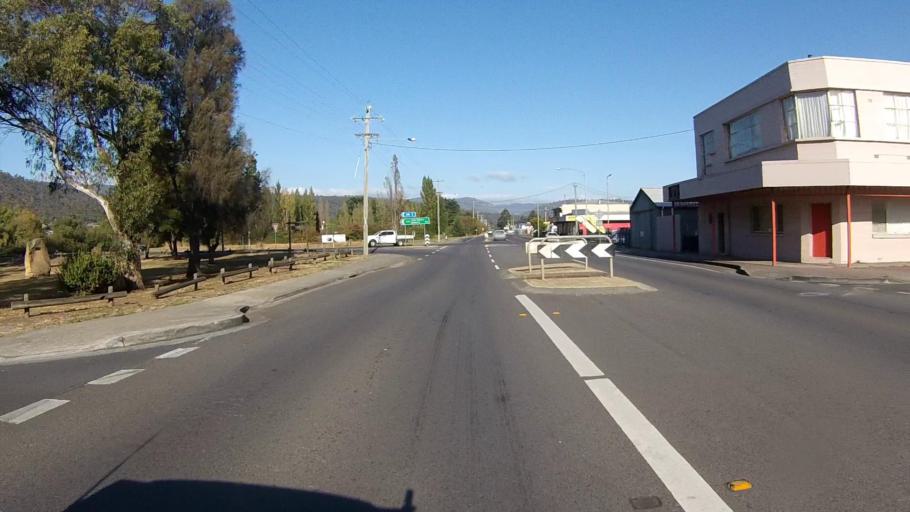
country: AU
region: Tasmania
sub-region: Derwent Valley
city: New Norfolk
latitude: -42.7770
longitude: 147.0559
